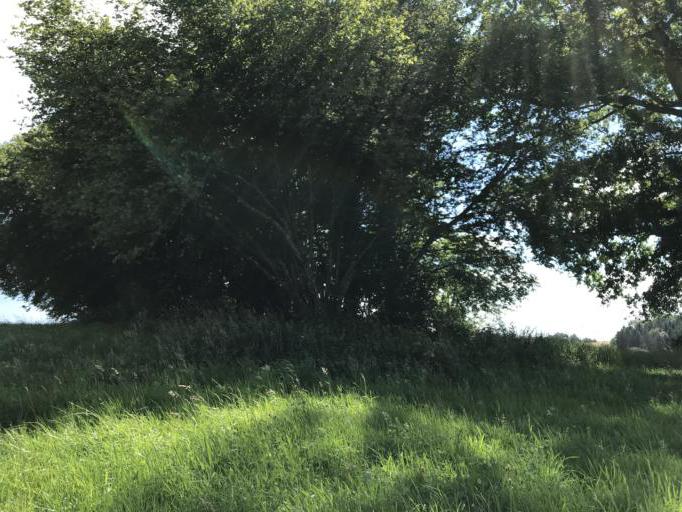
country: DE
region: Baden-Wuerttemberg
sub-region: Freiburg Region
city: Schopfheim
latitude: 47.6344
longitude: 7.8312
